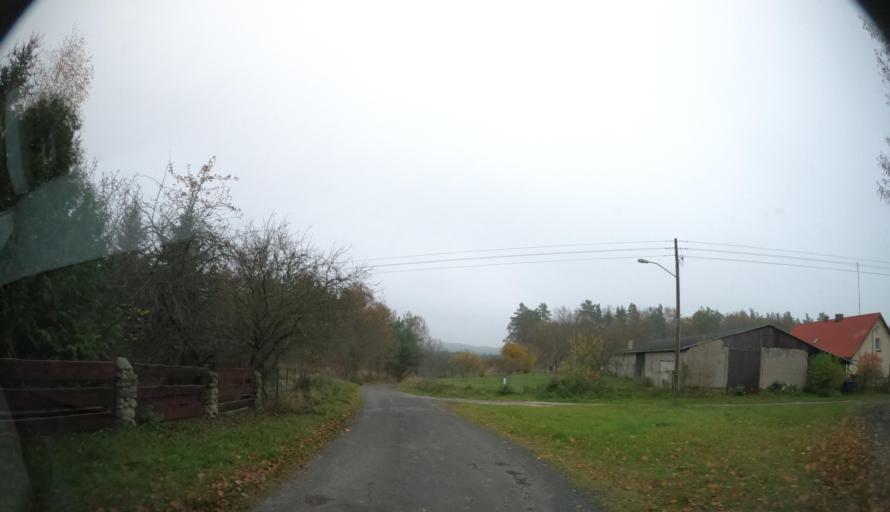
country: PL
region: West Pomeranian Voivodeship
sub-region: Powiat lobeski
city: Radowo Male
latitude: 53.6819
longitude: 15.4553
